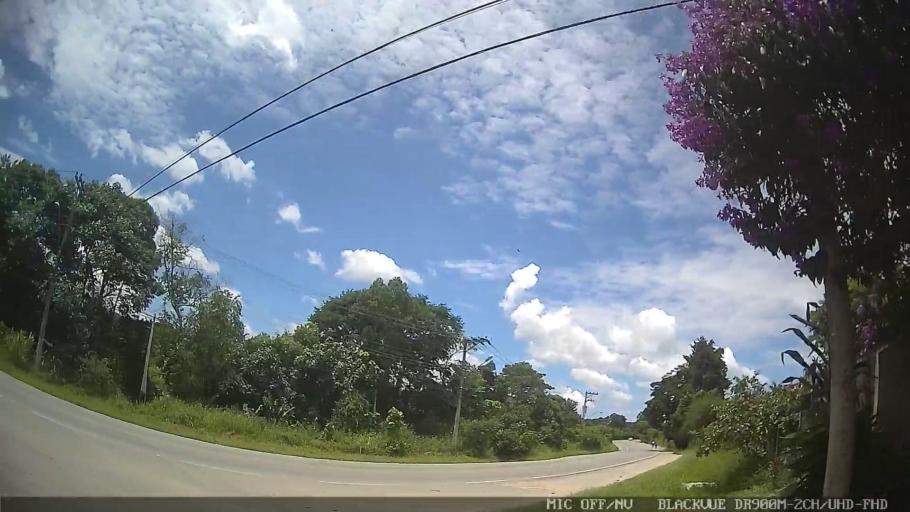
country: BR
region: Sao Paulo
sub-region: Biritiba-Mirim
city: Biritiba Mirim
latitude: -23.5486
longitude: -45.9620
